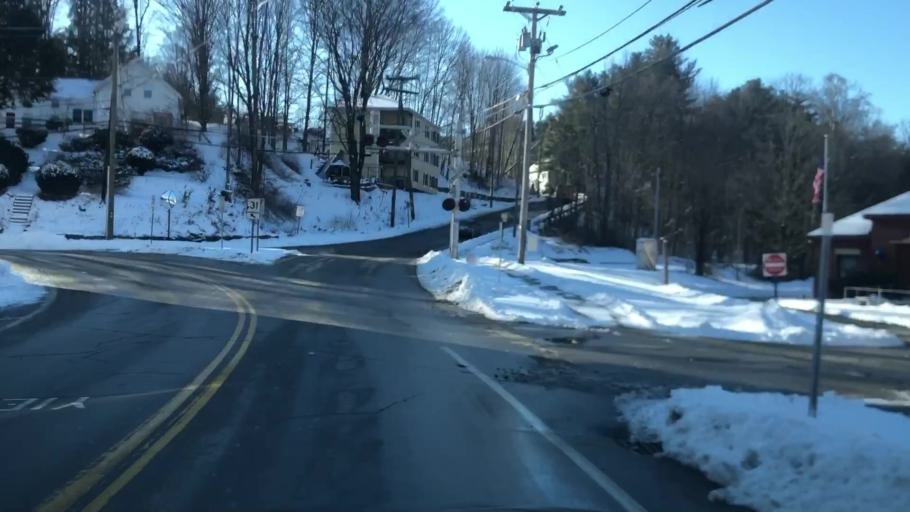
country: US
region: New Hampshire
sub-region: Hillsborough County
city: Wilton
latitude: 42.8446
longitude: -71.7392
